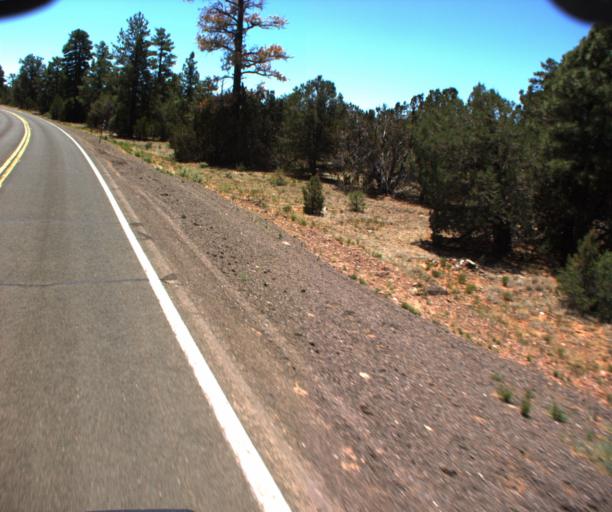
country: US
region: Arizona
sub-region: Gila County
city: Star Valley
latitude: 34.6762
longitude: -111.1118
